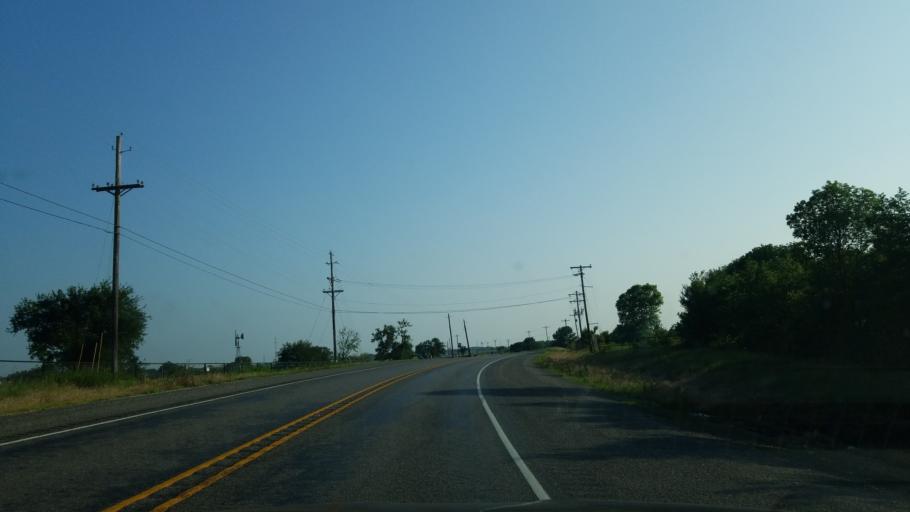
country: US
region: Texas
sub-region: Denton County
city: Denton
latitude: 33.2779
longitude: -97.0945
